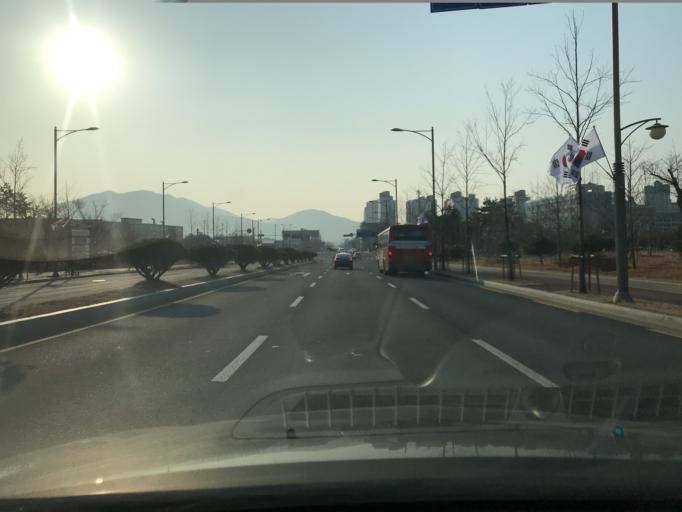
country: KR
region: Daegu
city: Hwawon
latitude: 35.6893
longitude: 128.4599
